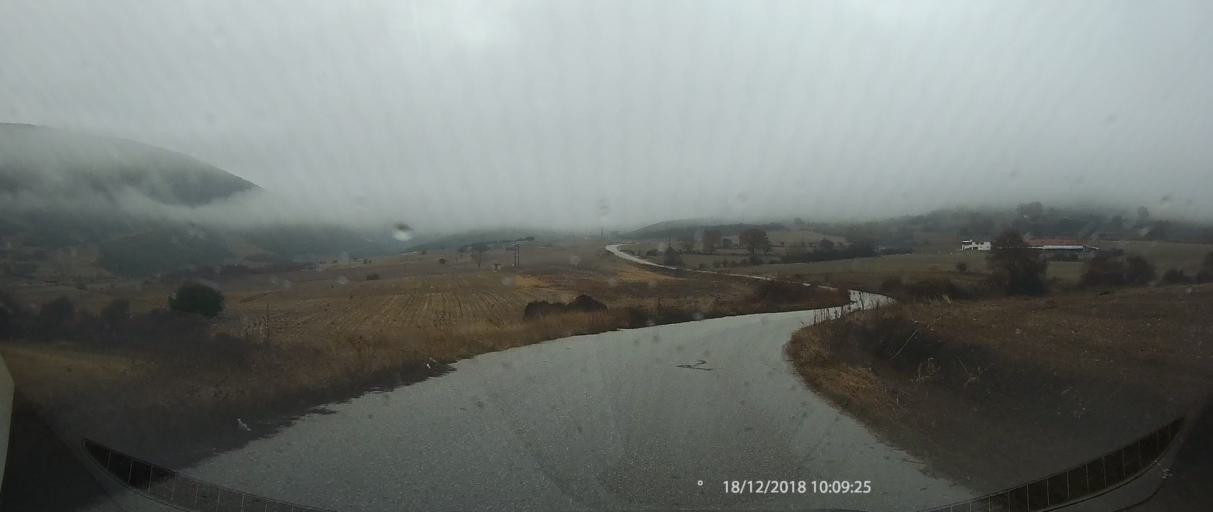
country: GR
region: Thessaly
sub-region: Nomos Larisis
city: Livadi
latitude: 40.0811
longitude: 22.2154
